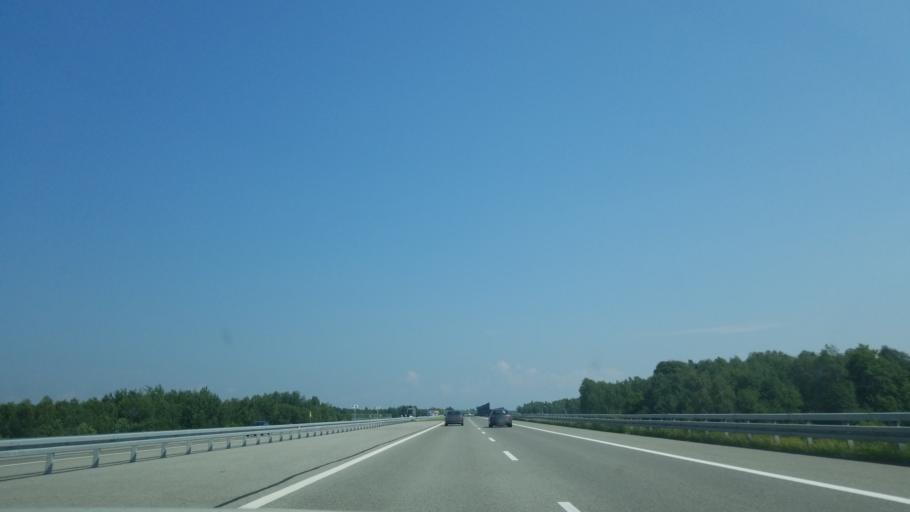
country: PL
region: Subcarpathian Voivodeship
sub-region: Powiat ropczycko-sedziszowski
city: Ostrow
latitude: 50.1071
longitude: 21.6296
